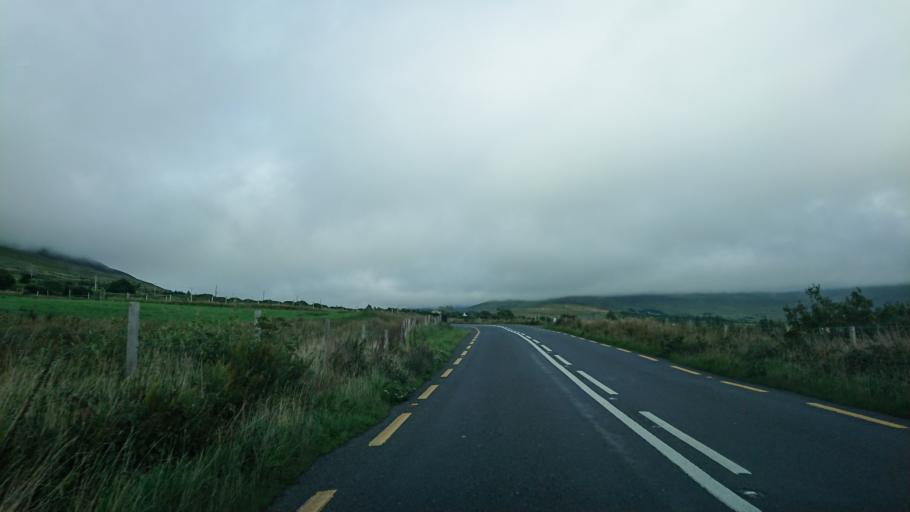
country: IE
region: Munster
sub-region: Ciarrai
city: Cahersiveen
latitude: 51.9894
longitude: -10.1363
